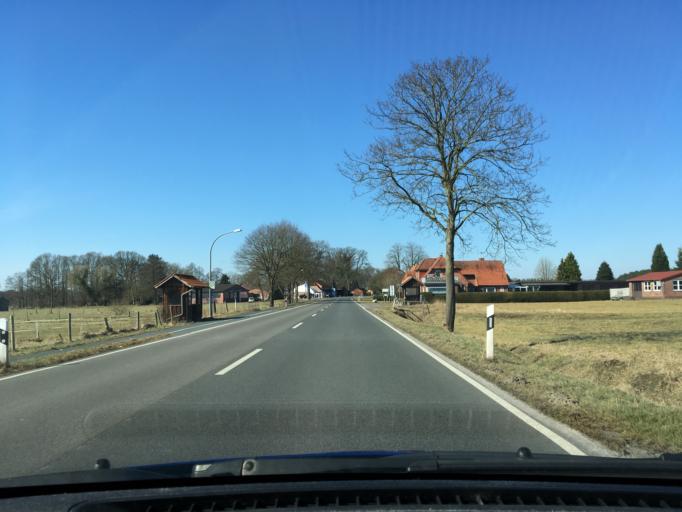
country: DE
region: Lower Saxony
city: Brockel
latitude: 53.0961
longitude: 9.5144
